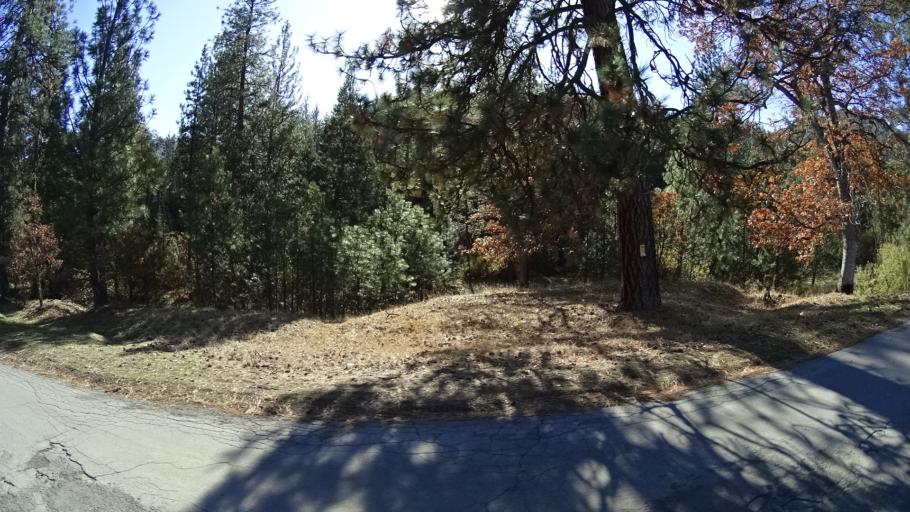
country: US
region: California
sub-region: Siskiyou County
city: Yreka
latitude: 41.7220
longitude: -122.6926
